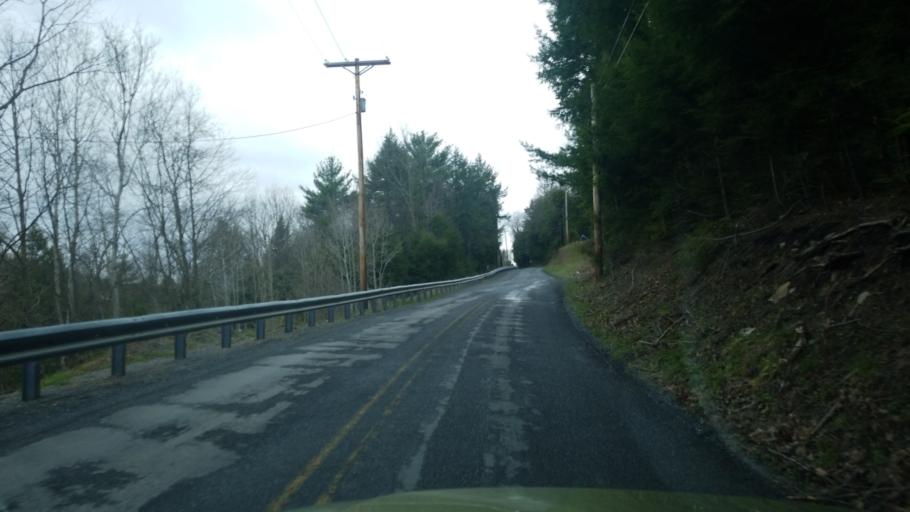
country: US
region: Pennsylvania
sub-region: Clearfield County
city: Clearfield
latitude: 41.0711
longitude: -78.4218
